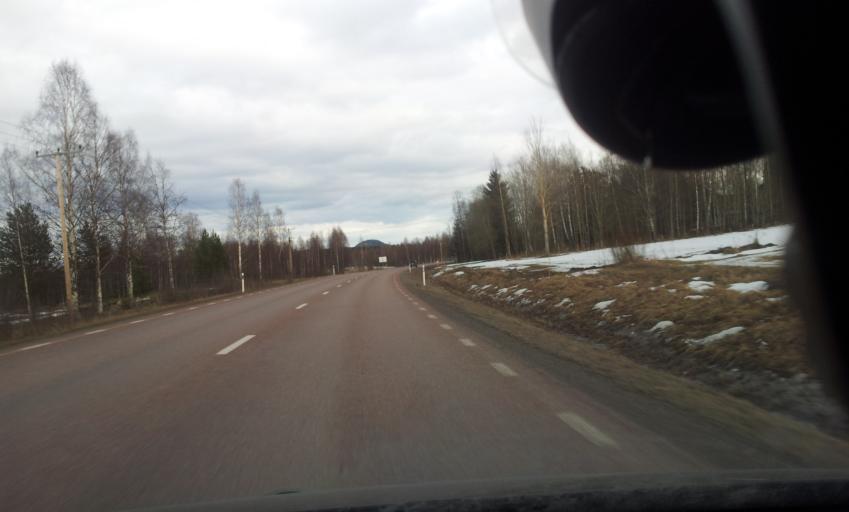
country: SE
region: Gaevleborg
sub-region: Ljusdals Kommun
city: Ljusdal
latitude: 61.8150
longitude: 16.0823
